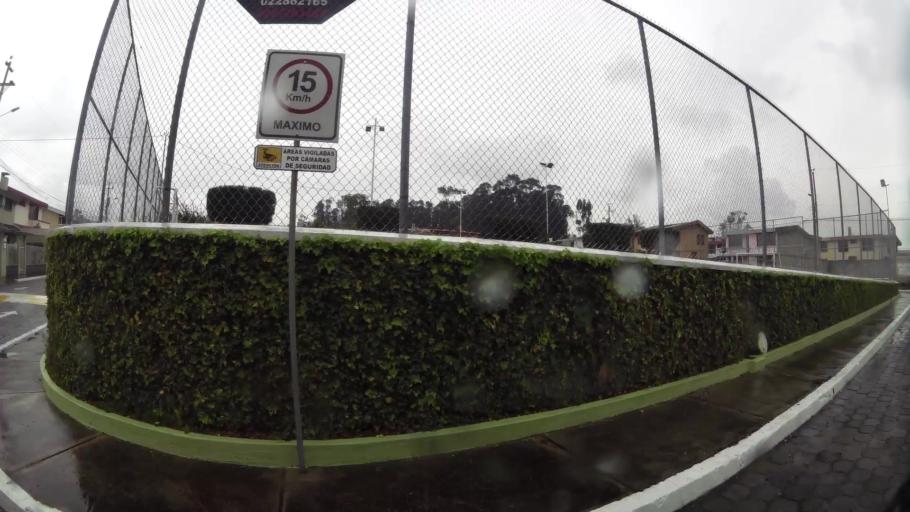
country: EC
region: Pichincha
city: Sangolqui
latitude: -0.3000
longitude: -78.4471
